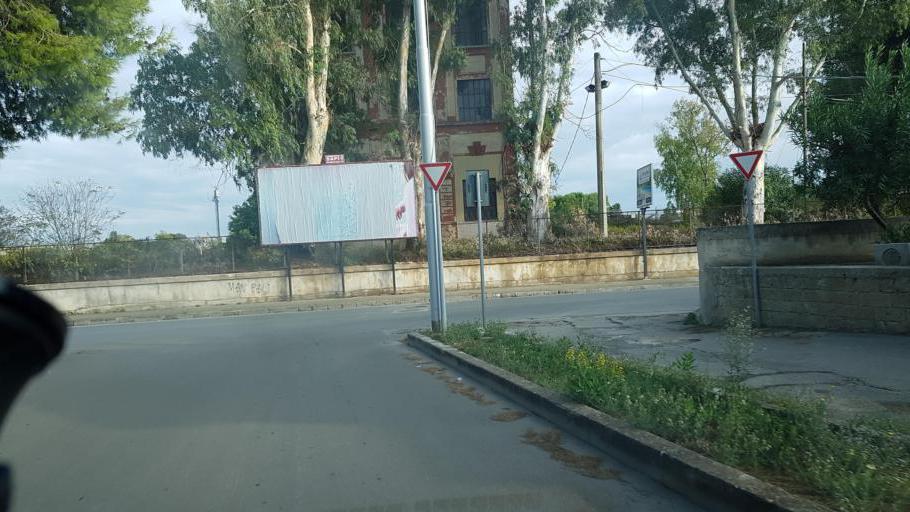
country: IT
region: Apulia
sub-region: Provincia di Brindisi
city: Francavilla Fontana
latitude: 40.5360
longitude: 17.5886
